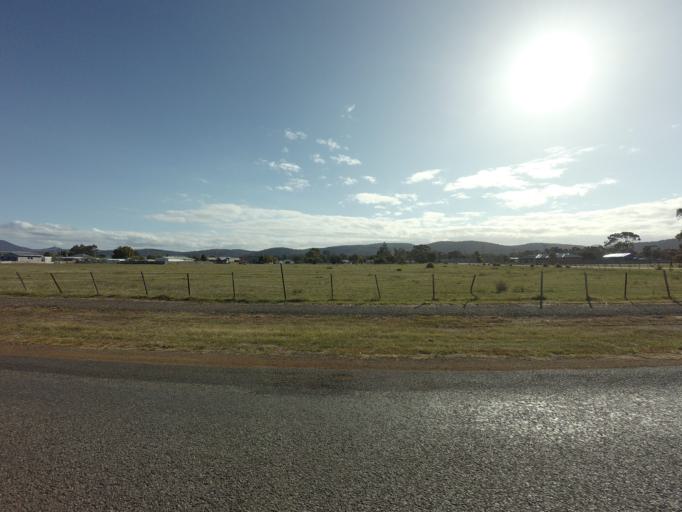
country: AU
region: Tasmania
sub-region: Sorell
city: Sorell
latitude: -42.5041
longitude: 147.9157
